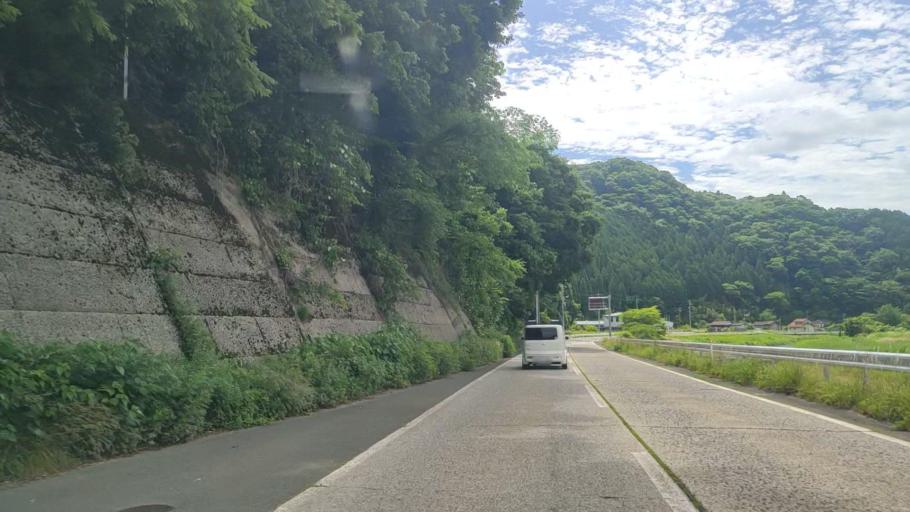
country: JP
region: Okayama
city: Niimi
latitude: 35.1720
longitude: 133.5768
